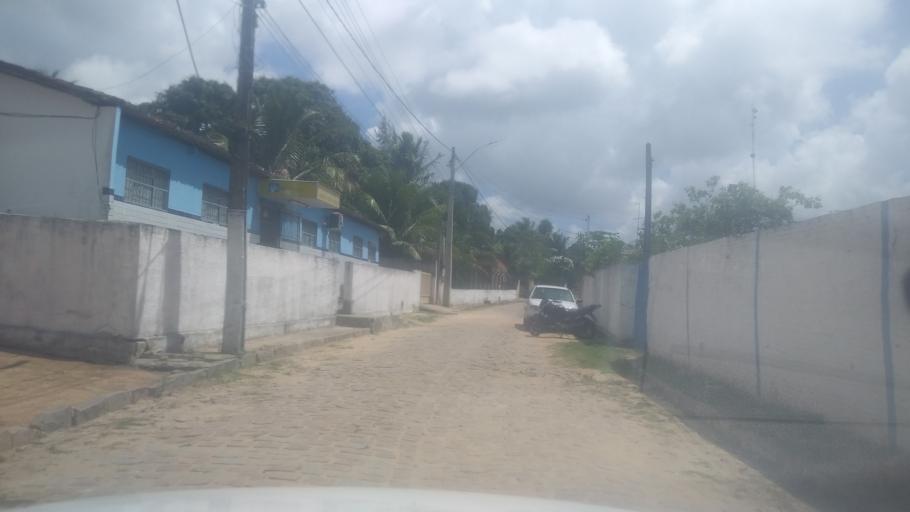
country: BR
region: Rio Grande do Norte
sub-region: Sao Jose De Mipibu
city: Sao Jose de Mipibu
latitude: -6.0702
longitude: -35.2288
